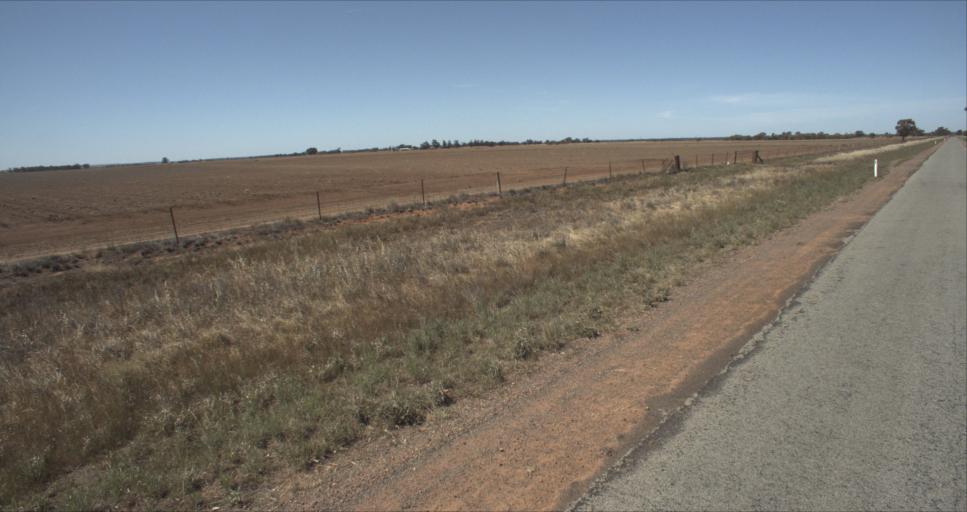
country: AU
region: New South Wales
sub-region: Leeton
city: Leeton
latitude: -34.5601
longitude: 146.3129
